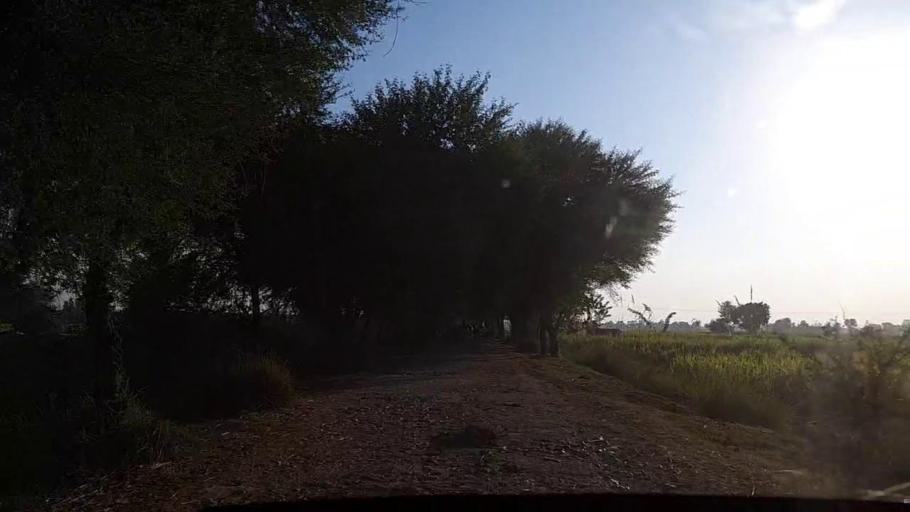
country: PK
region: Sindh
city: Sobhadero
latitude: 27.4088
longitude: 68.3935
